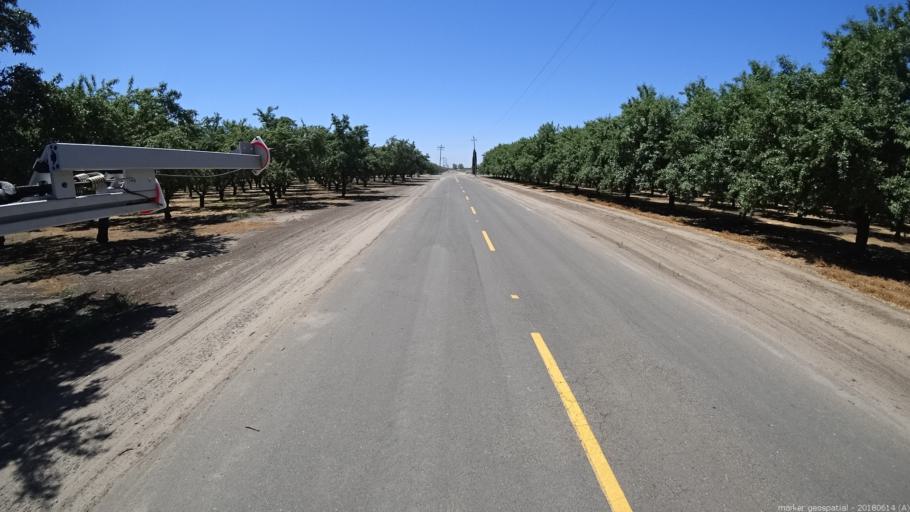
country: US
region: California
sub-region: Madera County
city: Fairmead
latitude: 36.9974
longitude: -120.2476
